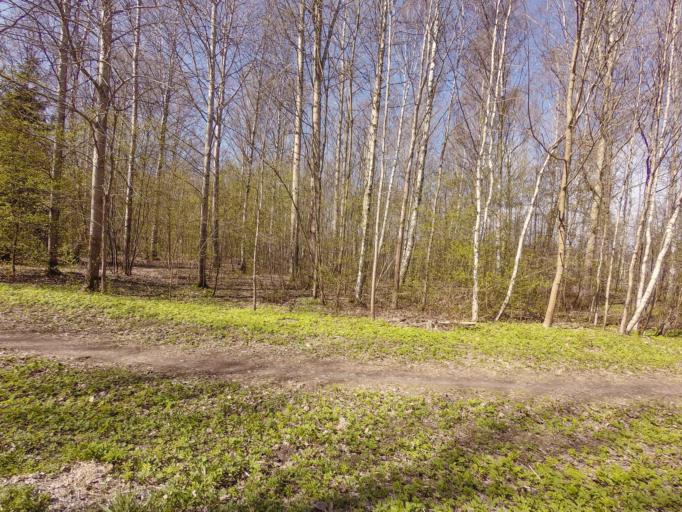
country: FI
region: Uusimaa
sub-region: Helsinki
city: Vantaa
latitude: 60.2234
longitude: 25.0888
